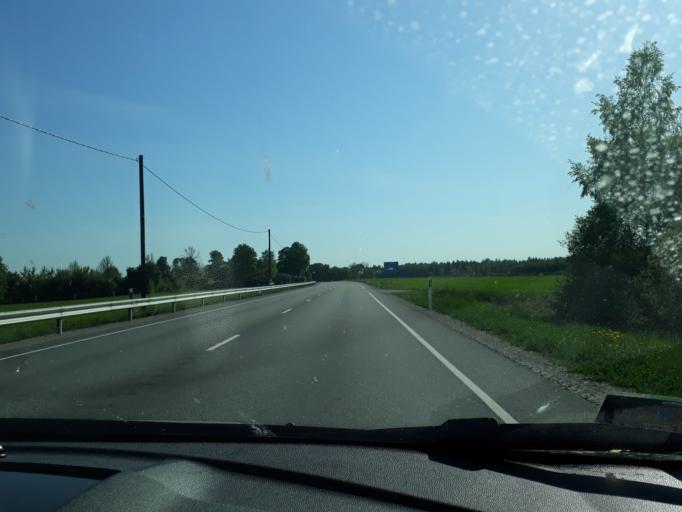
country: EE
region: Paernumaa
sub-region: Tootsi vald
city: Tootsi
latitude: 58.5565
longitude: 24.8603
